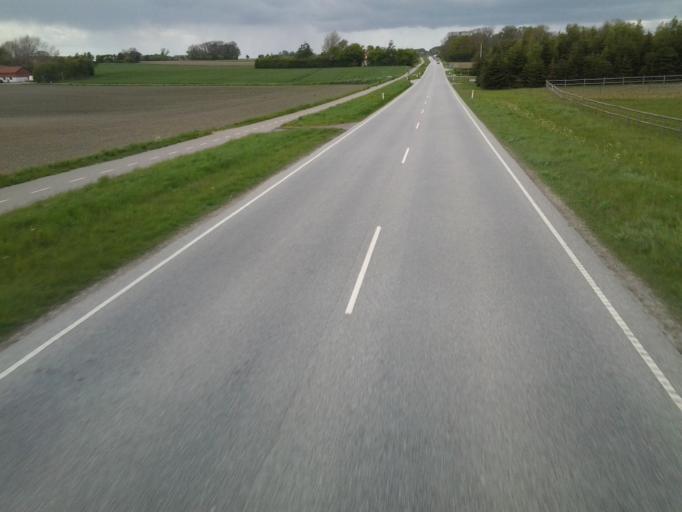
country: DK
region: Zealand
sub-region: Guldborgsund Kommune
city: Nykobing Falster
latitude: 54.6939
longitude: 11.9120
